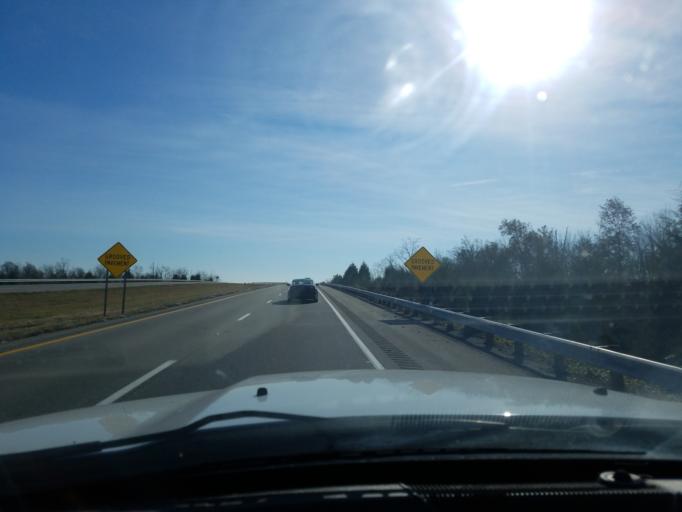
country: US
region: Ohio
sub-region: Adams County
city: Winchester
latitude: 38.9397
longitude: -83.6707
